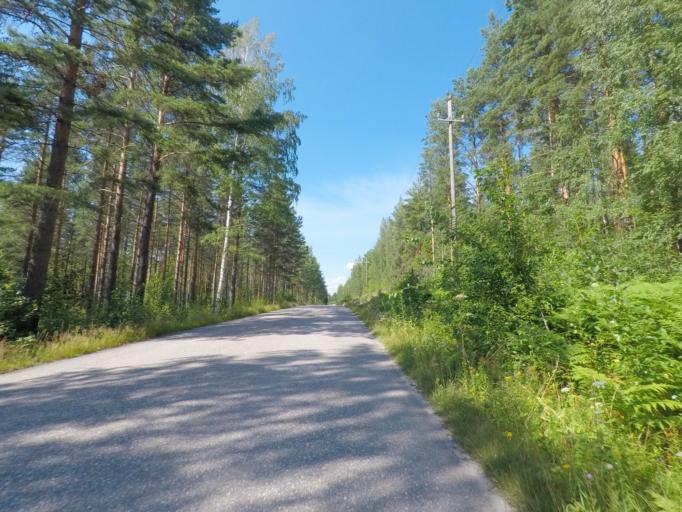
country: FI
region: Southern Savonia
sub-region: Mikkeli
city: Puumala
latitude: 61.4426
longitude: 28.1643
